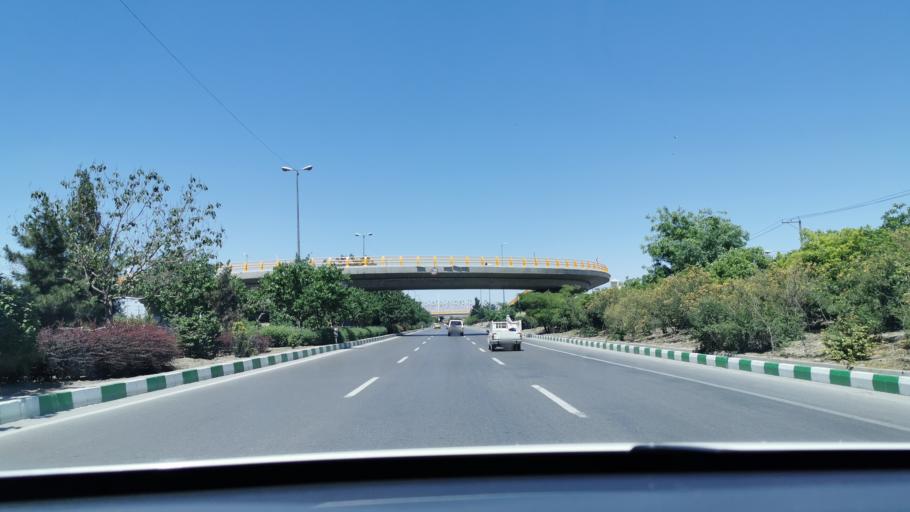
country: IR
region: Razavi Khorasan
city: Mashhad
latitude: 36.2663
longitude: 59.6542
